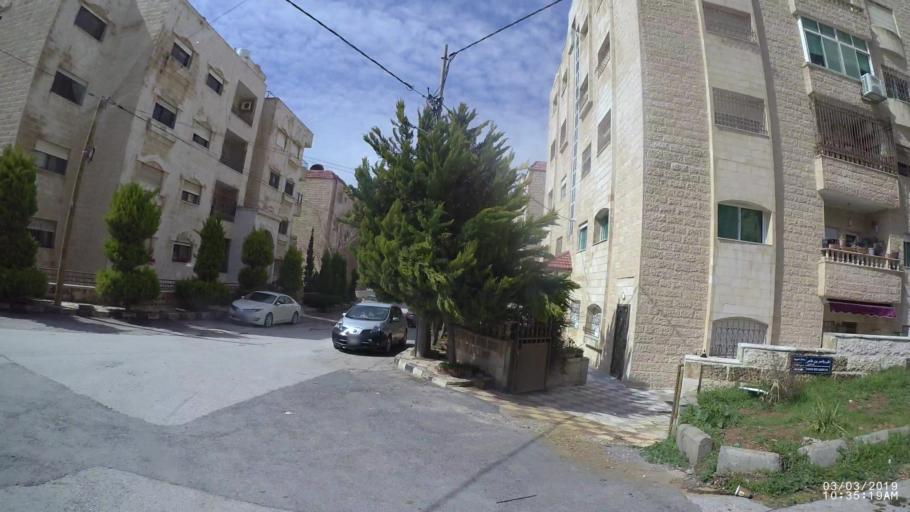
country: JO
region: Amman
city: Al Jubayhah
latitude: 31.9971
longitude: 35.9069
